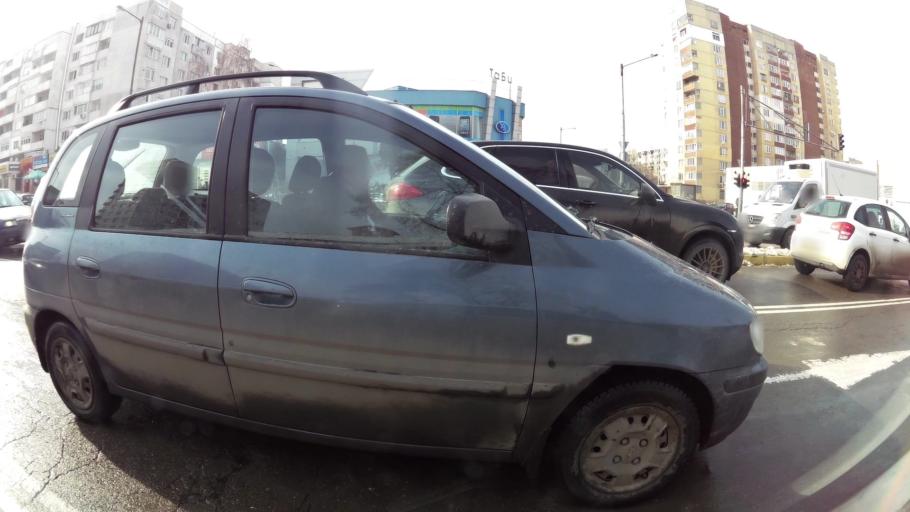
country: BG
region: Sofia-Capital
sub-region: Stolichna Obshtina
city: Sofia
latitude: 42.7021
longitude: 23.3600
